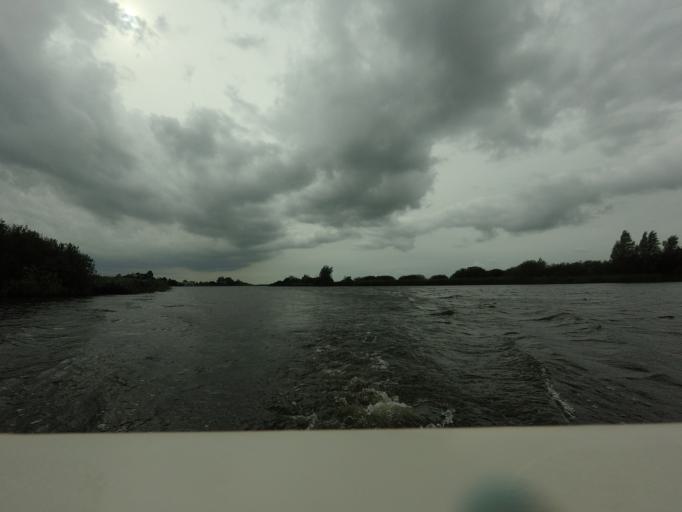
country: NL
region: Friesland
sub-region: Gemeente Boarnsterhim
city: Aldeboarn
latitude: 53.0973
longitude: 5.9407
